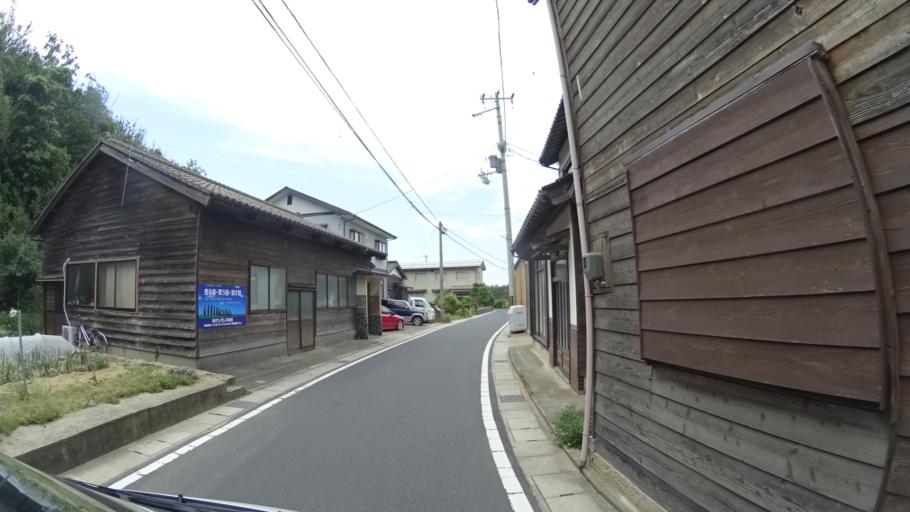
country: JP
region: Kyoto
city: Miyazu
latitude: 35.7004
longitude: 135.0530
